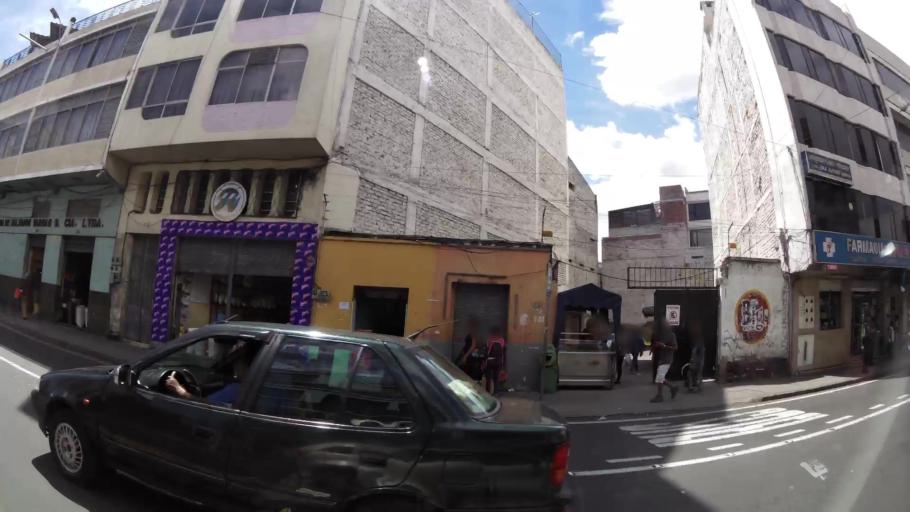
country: EC
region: Tungurahua
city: Ambato
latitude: -1.2414
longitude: -78.6243
